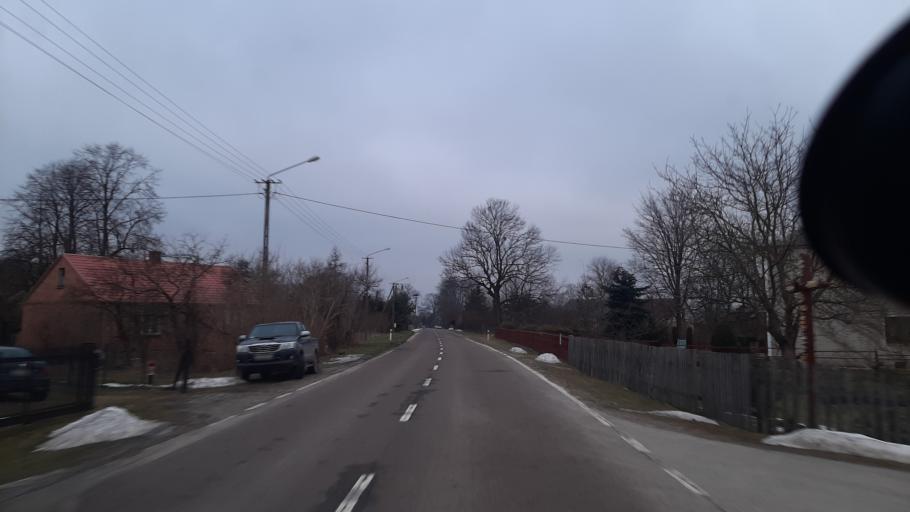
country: PL
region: Lublin Voivodeship
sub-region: Powiat parczewski
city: Podedworze
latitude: 51.5920
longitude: 23.1905
